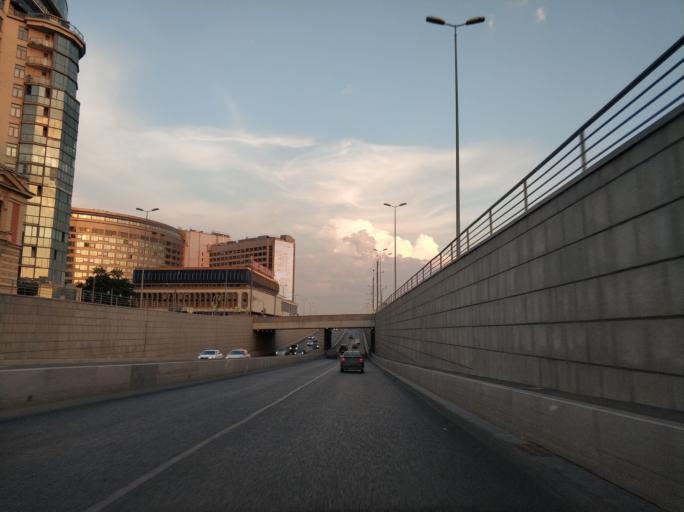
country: RU
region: Leningrad
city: Sampsonievskiy
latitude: 59.9591
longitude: 30.3388
